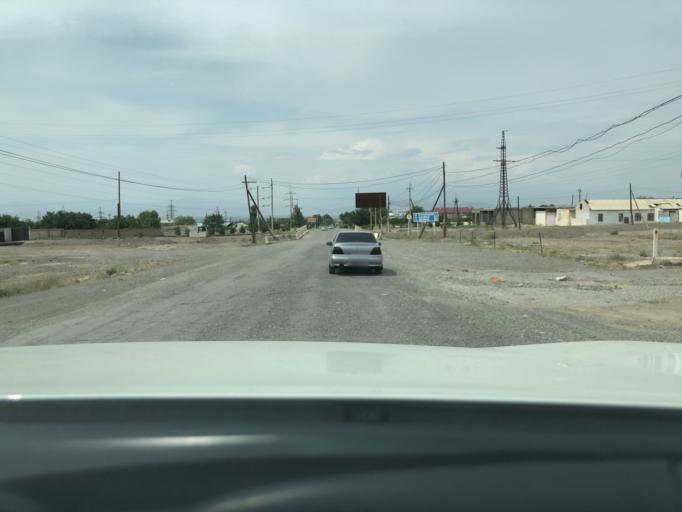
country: TJ
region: Viloyati Sughd
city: Konibodom
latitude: 40.2735
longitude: 70.4468
